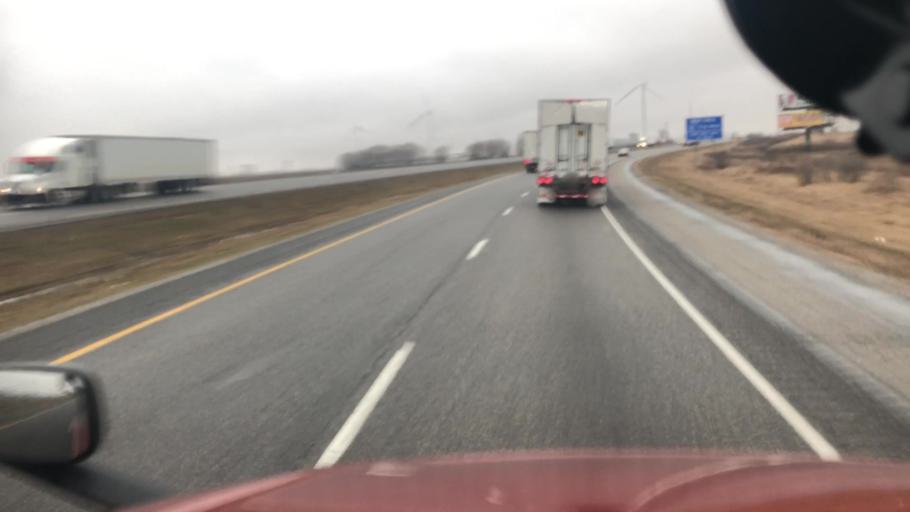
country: US
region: Indiana
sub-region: White County
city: Wolcott
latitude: 40.6737
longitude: -87.0515
